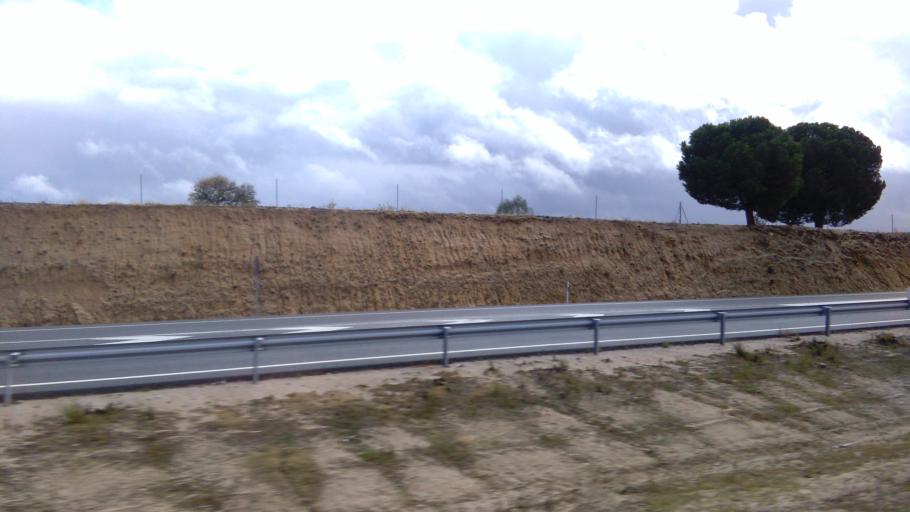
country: ES
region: Castille-La Mancha
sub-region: Province of Toledo
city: Valmojado
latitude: 40.2049
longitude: -4.1029
